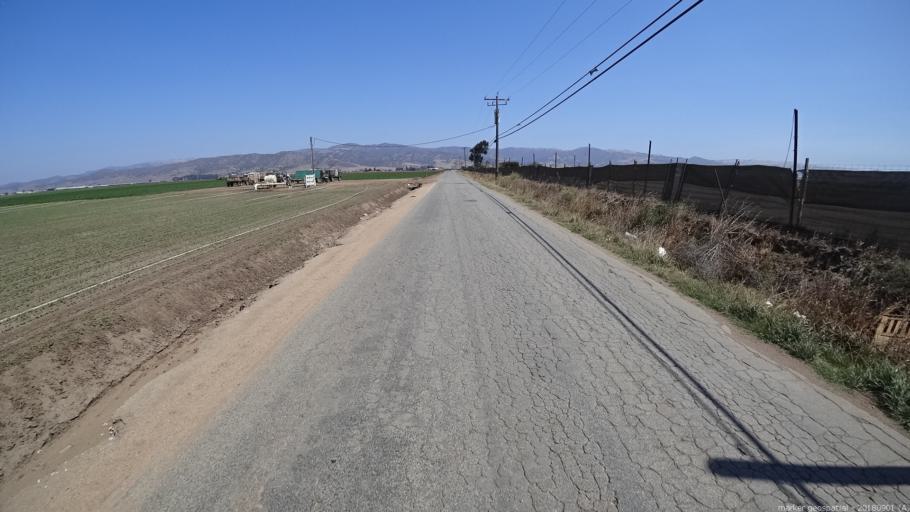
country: US
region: California
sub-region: Monterey County
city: Chualar
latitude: 36.6150
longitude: -121.5432
